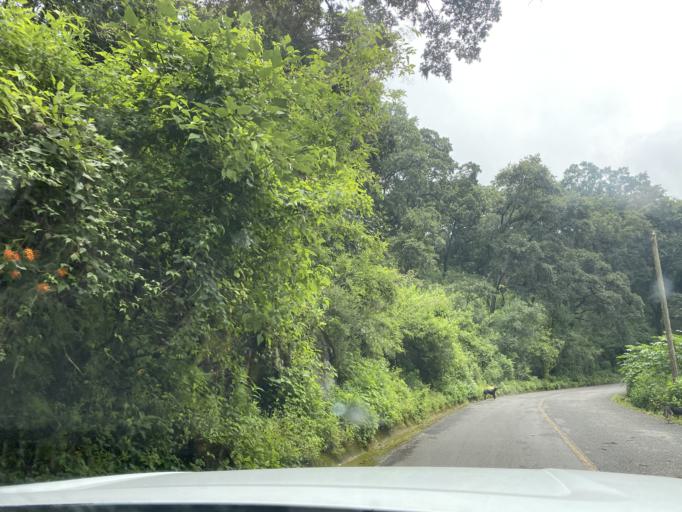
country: MX
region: Morelos
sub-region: Yecapixtla
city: Achichipico
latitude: 18.9396
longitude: -98.8170
